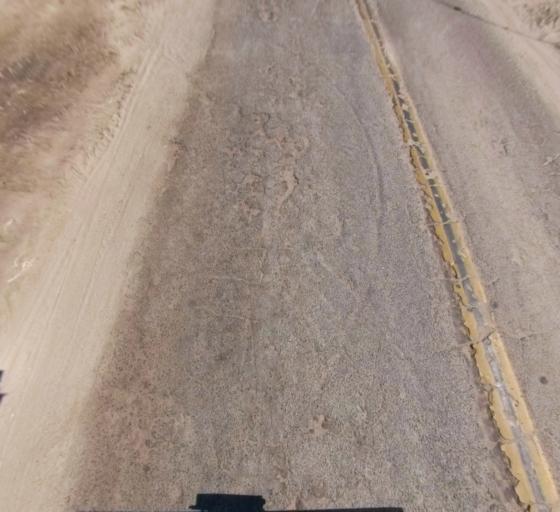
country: US
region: California
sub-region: Madera County
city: Parkwood
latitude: 36.8657
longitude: -120.0375
